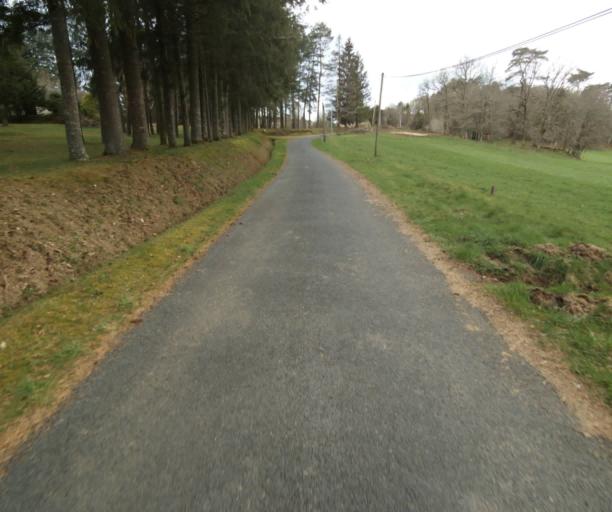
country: FR
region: Limousin
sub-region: Departement de la Correze
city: Correze
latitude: 45.2687
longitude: 1.9648
